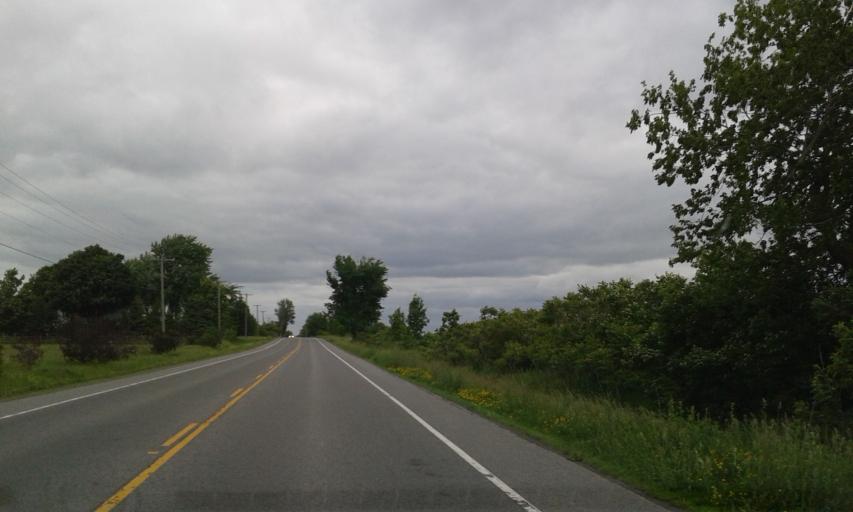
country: CA
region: Ontario
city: Napanee Downtown
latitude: 44.1187
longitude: -76.9050
